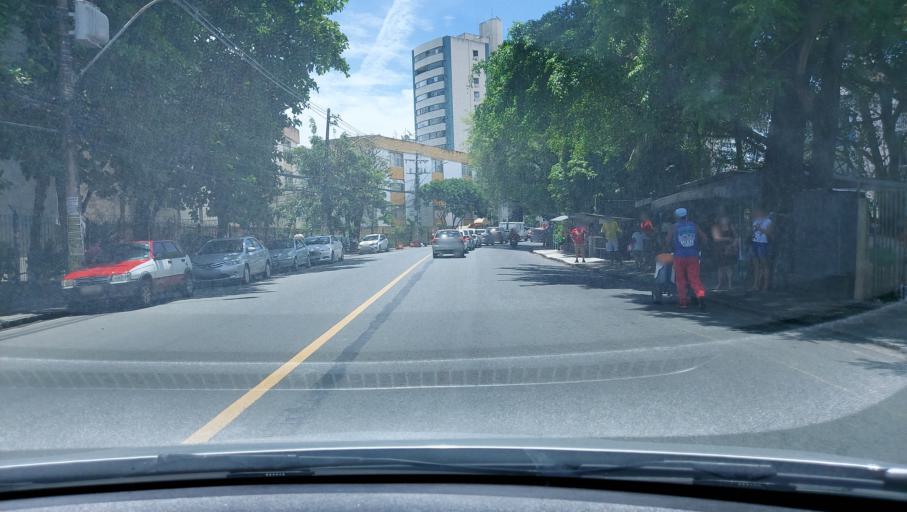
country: BR
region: Bahia
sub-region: Salvador
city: Salvador
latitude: -12.9906
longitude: -38.4836
